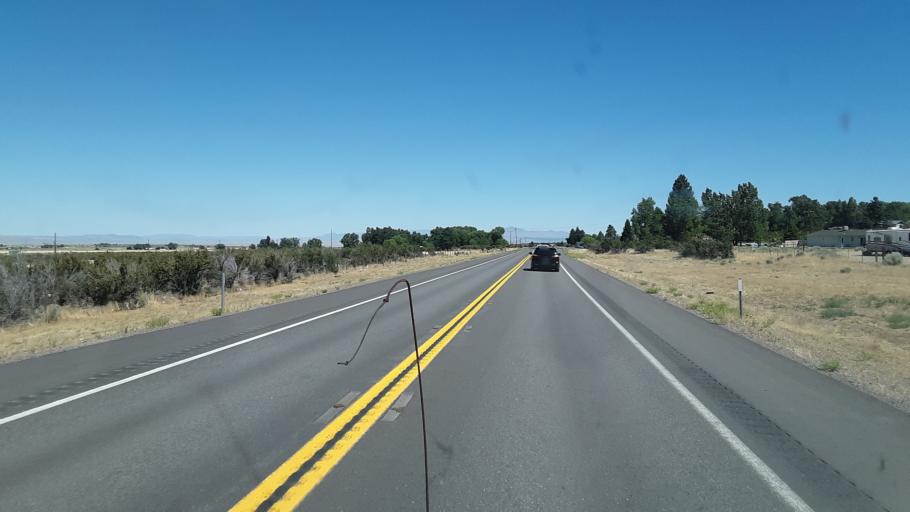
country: US
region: California
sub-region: Lassen County
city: Janesville
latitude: 40.2925
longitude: -120.5057
